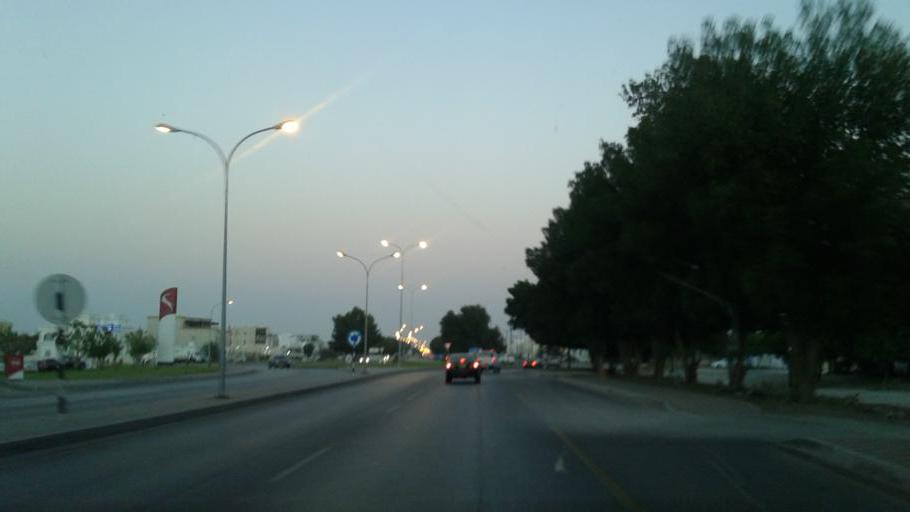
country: OM
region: Muhafazat Masqat
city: As Sib al Jadidah
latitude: 23.6144
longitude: 58.2182
